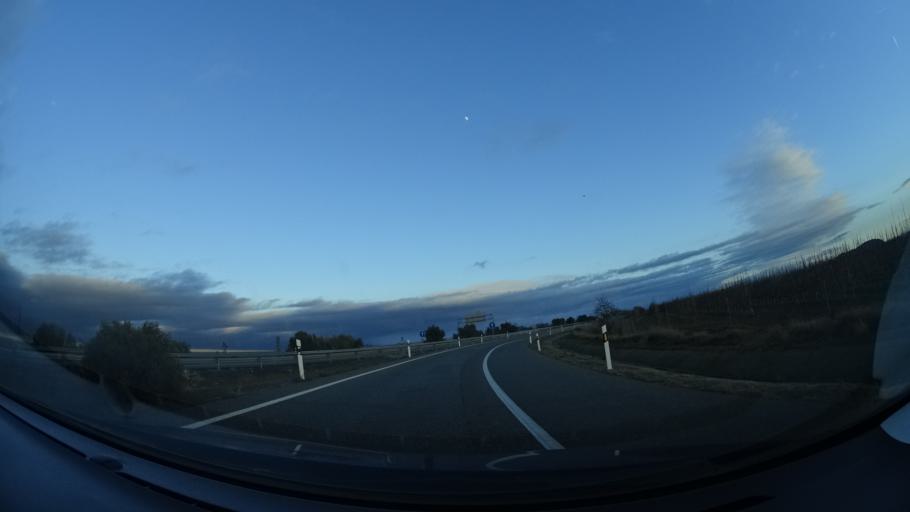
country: ES
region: Catalonia
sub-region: Provincia de Lleida
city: Alfes
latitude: 41.5493
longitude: 0.6223
